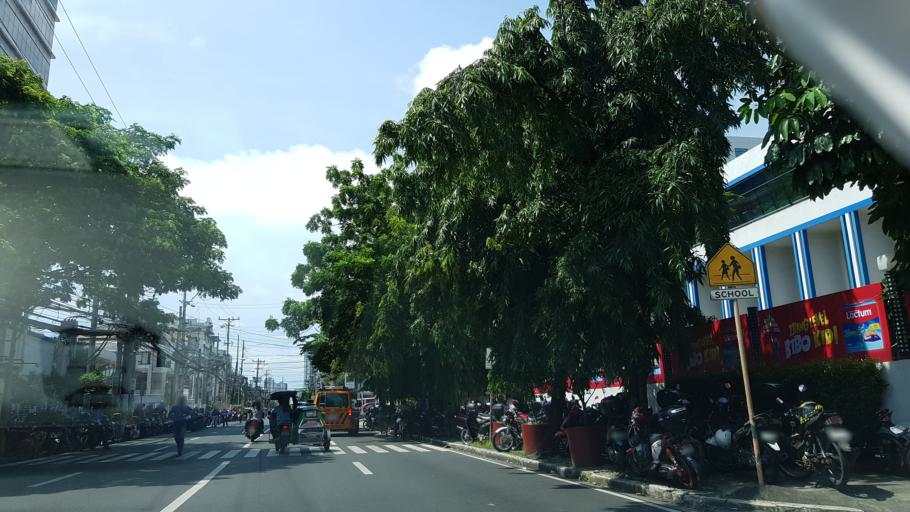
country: PH
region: Metro Manila
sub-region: Makati City
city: Makati City
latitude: 14.5324
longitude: 121.0232
